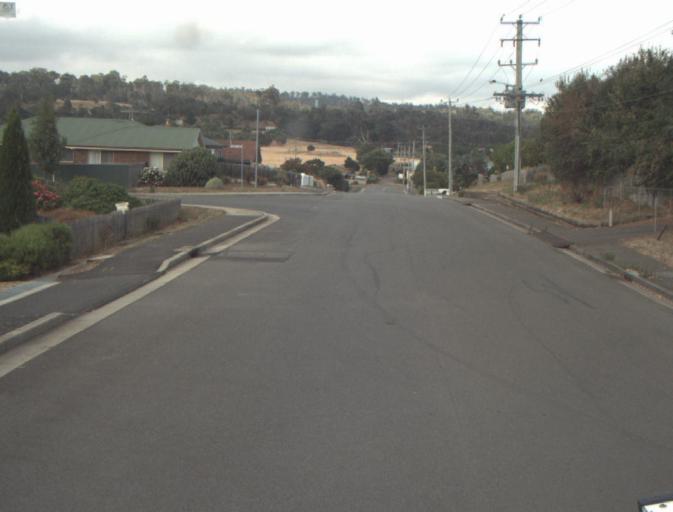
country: AU
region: Tasmania
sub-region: Launceston
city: Summerhill
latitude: -41.4829
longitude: 147.1623
